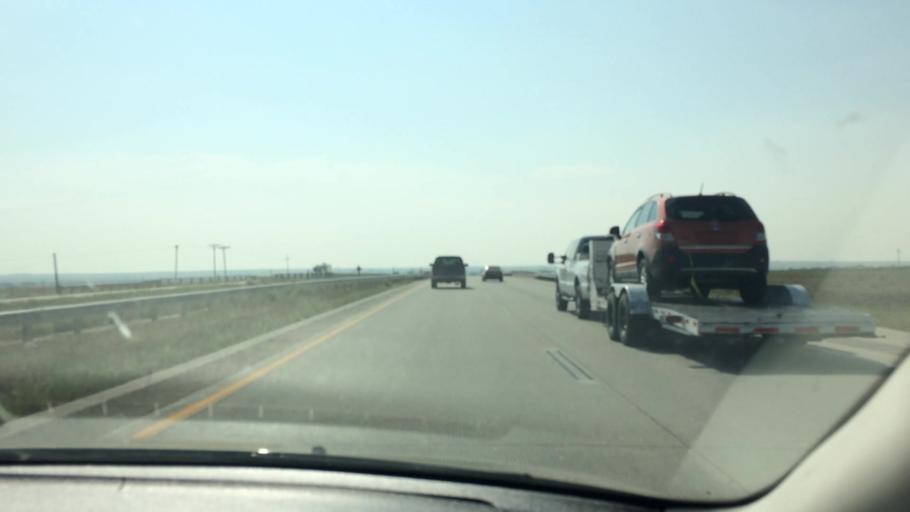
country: US
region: Colorado
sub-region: Adams County
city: Bennett
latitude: 39.7395
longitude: -104.5633
